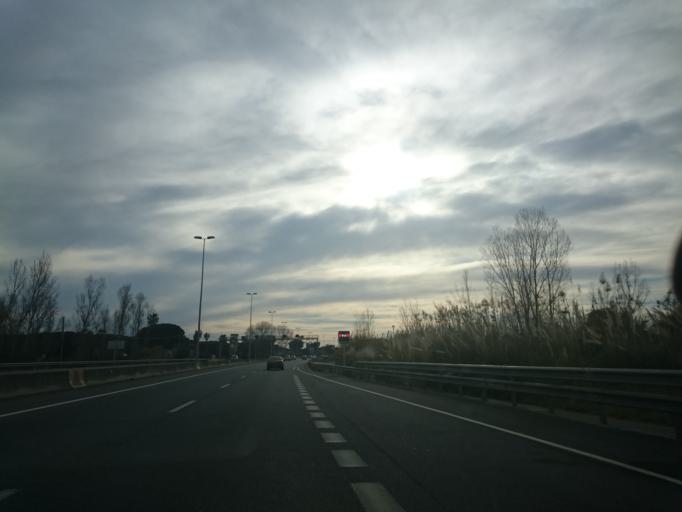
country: ES
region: Catalonia
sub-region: Provincia de Barcelona
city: Viladecans
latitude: 41.2767
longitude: 2.0494
